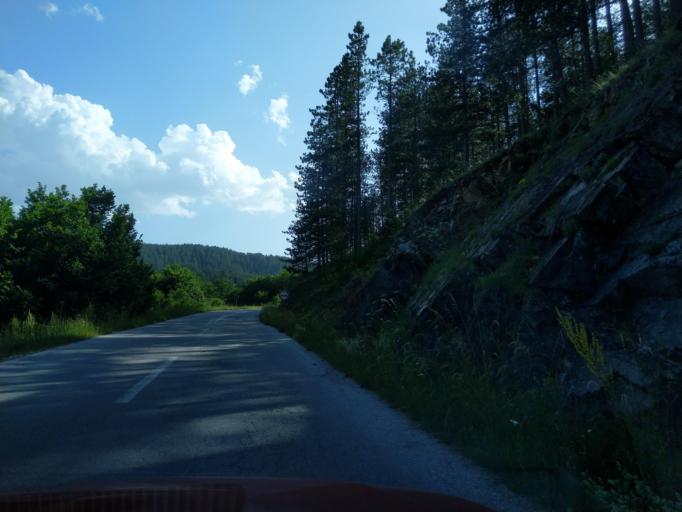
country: RS
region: Central Serbia
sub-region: Zlatiborski Okrug
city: Bajina Basta
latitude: 43.8494
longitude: 19.6205
